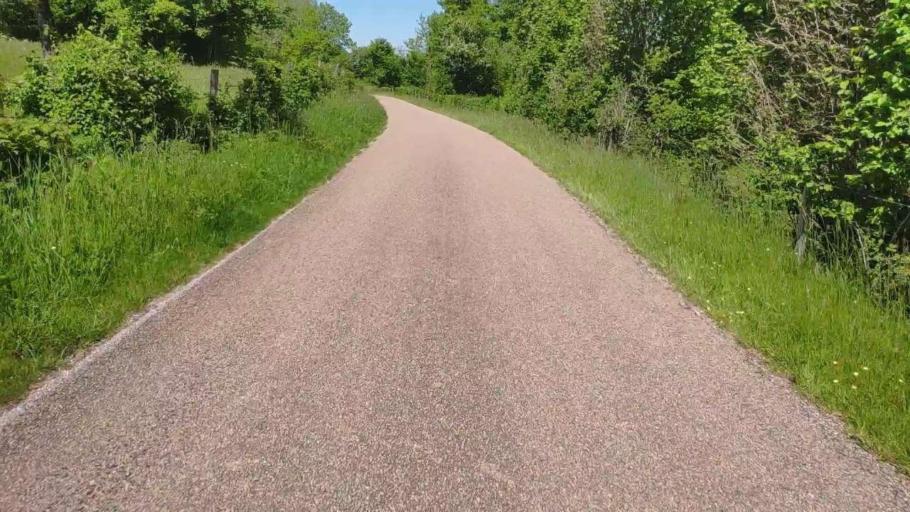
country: FR
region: Franche-Comte
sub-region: Departement du Jura
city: Poligny
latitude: 46.7339
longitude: 5.7243
